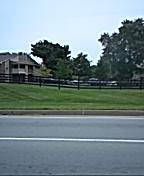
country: US
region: Kentucky
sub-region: Jefferson County
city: Hurstbourne
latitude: 38.2333
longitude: -85.5770
